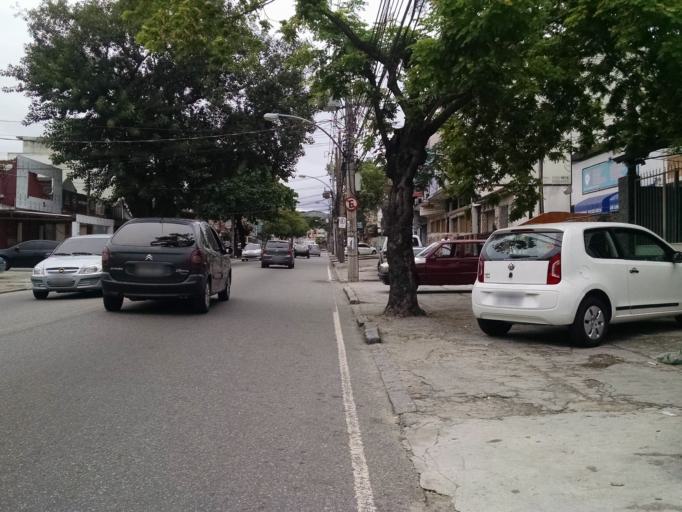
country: BR
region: Rio de Janeiro
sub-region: Duque De Caxias
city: Duque de Caxias
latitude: -22.8313
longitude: -43.3191
